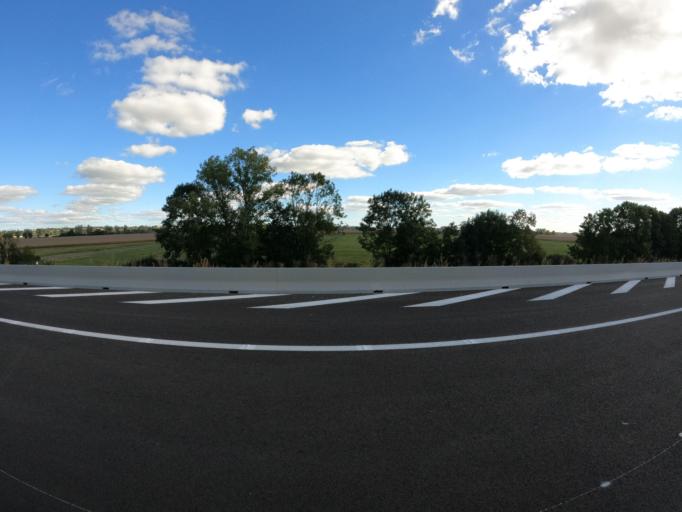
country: FR
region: Auvergne
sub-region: Departement de l'Allier
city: Toulon-sur-Allier
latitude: 46.4877
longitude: 3.3433
